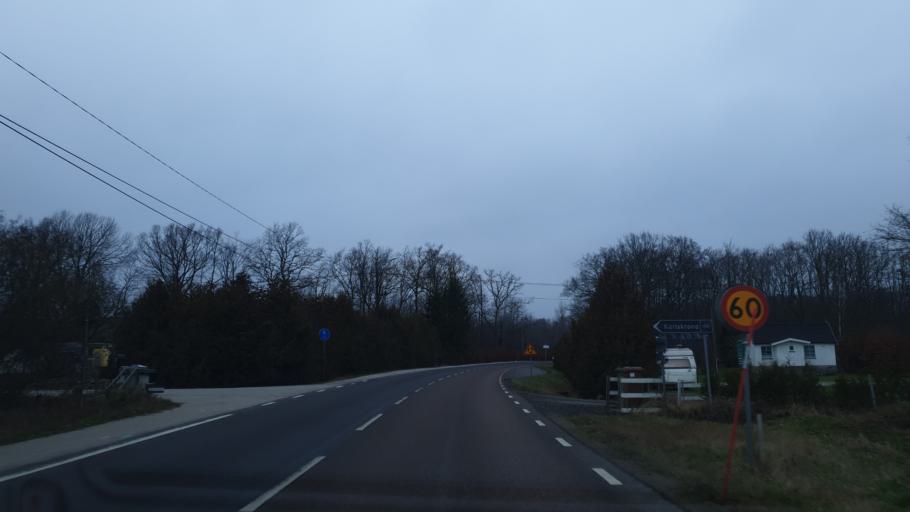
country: SE
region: Blekinge
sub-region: Karlskrona Kommun
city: Jaemjoe
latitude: 56.1828
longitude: 15.7198
